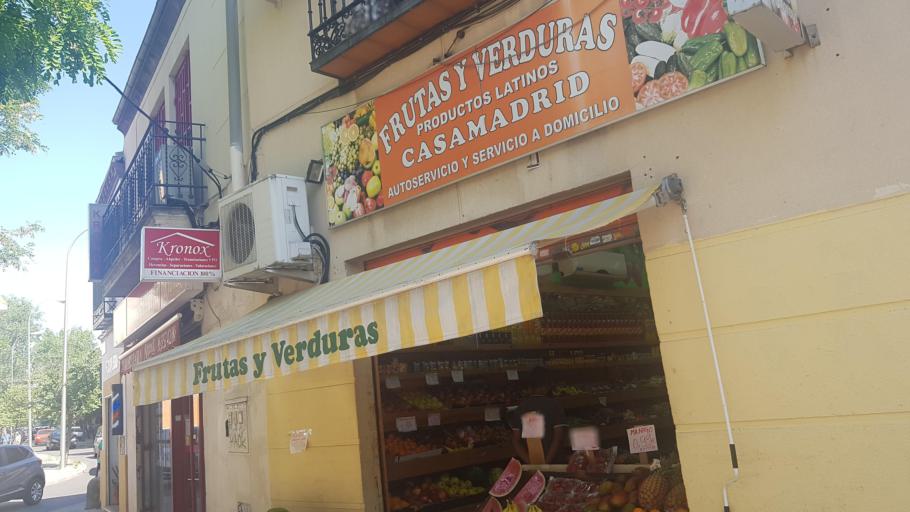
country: ES
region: Madrid
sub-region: Provincia de Madrid
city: Villa de Vallecas
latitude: 40.3802
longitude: -3.6222
